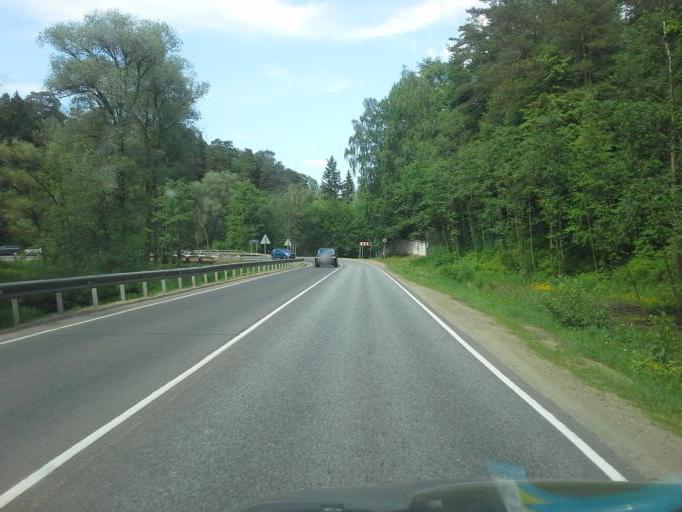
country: RU
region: Moskovskaya
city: Gorki Vtoryye
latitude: 55.7194
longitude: 37.1924
